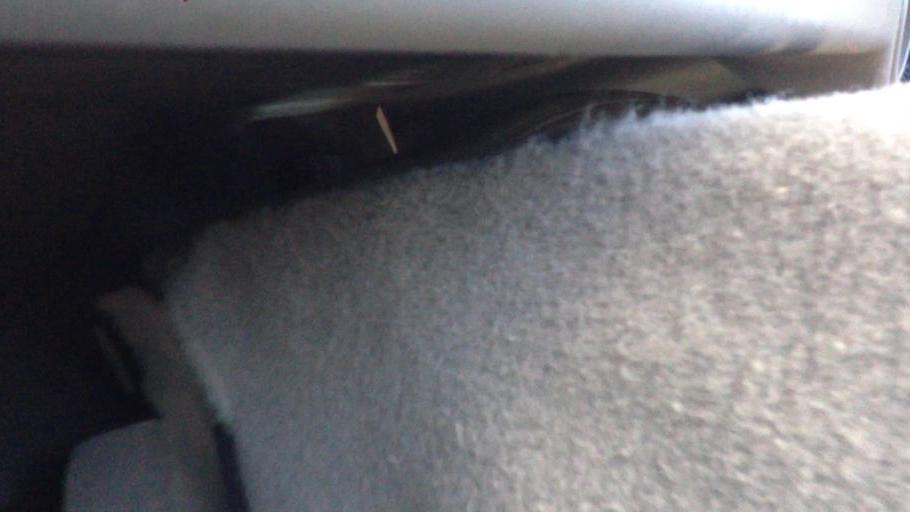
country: US
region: New York
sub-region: Columbia County
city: Oakdale
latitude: 42.2415
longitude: -73.7812
